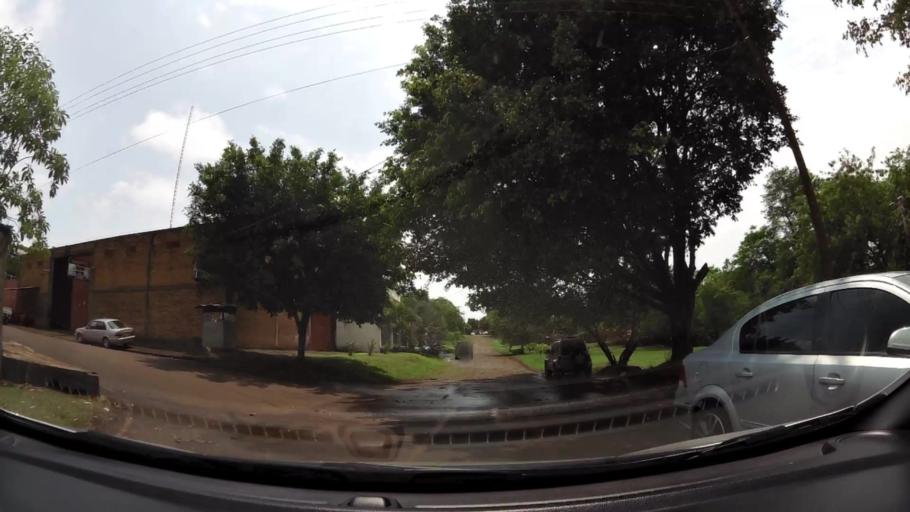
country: PY
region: Alto Parana
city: Ciudad del Este
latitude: -25.5054
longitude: -54.6554
